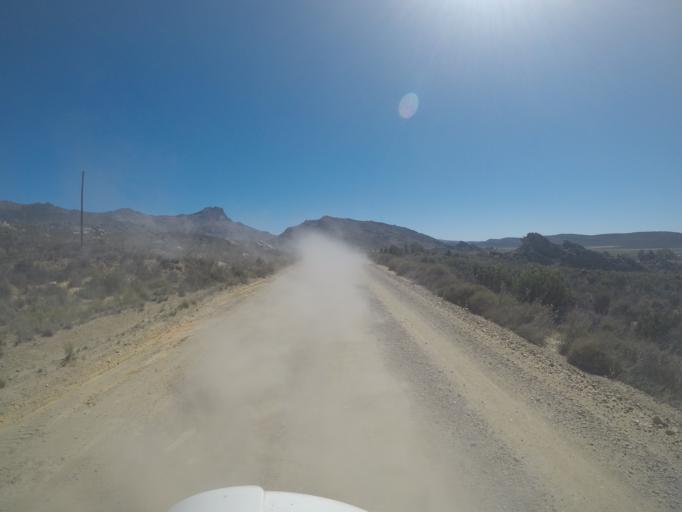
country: ZA
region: Western Cape
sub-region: Cape Winelands District Municipality
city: Ceres
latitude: -32.8734
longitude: 19.4450
